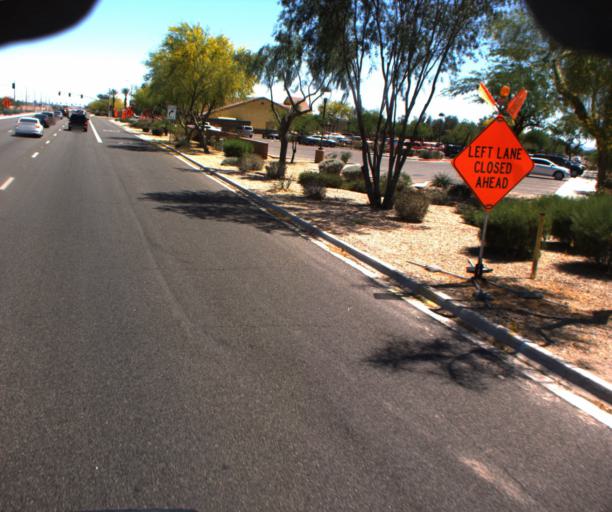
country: US
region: Arizona
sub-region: Maricopa County
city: Sun City West
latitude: 33.6457
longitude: -112.3596
